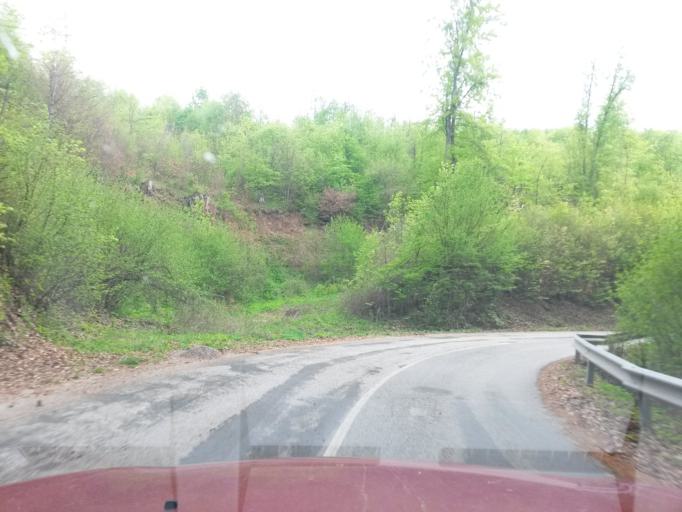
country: SK
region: Kosicky
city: Roznava
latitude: 48.5631
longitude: 20.4790
